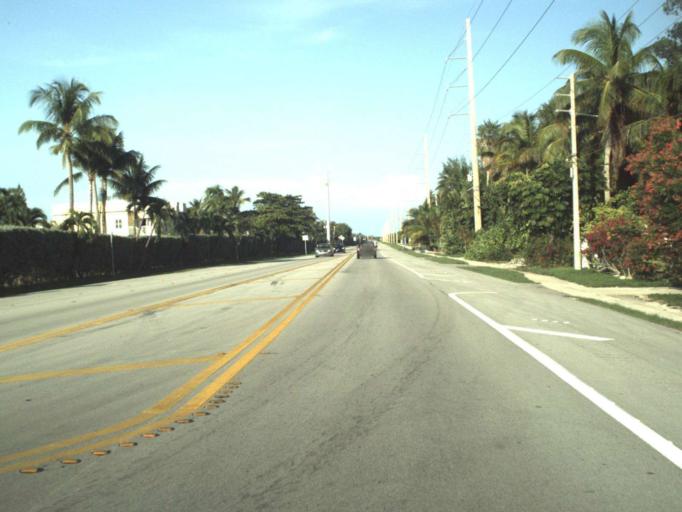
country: US
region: Florida
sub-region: Monroe County
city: Islamorada
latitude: 24.8050
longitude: -80.8451
